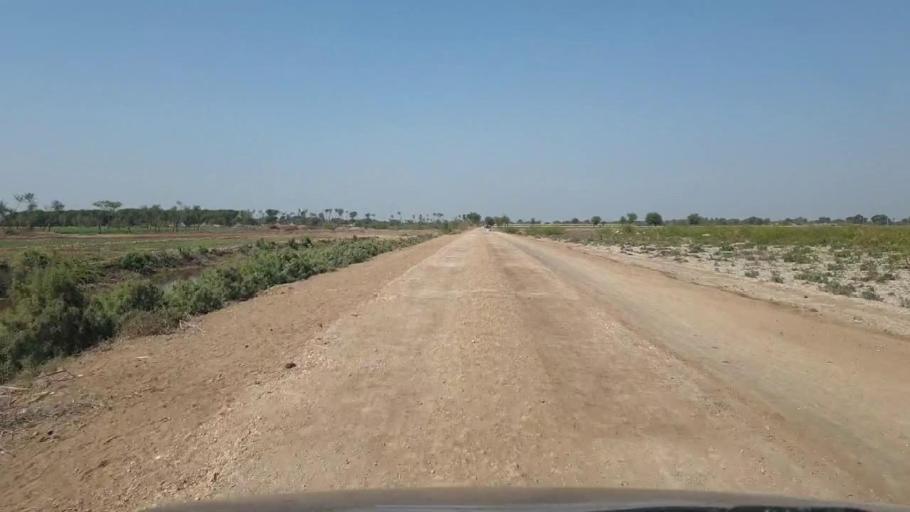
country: PK
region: Sindh
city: Samaro
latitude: 25.2323
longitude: 69.2797
